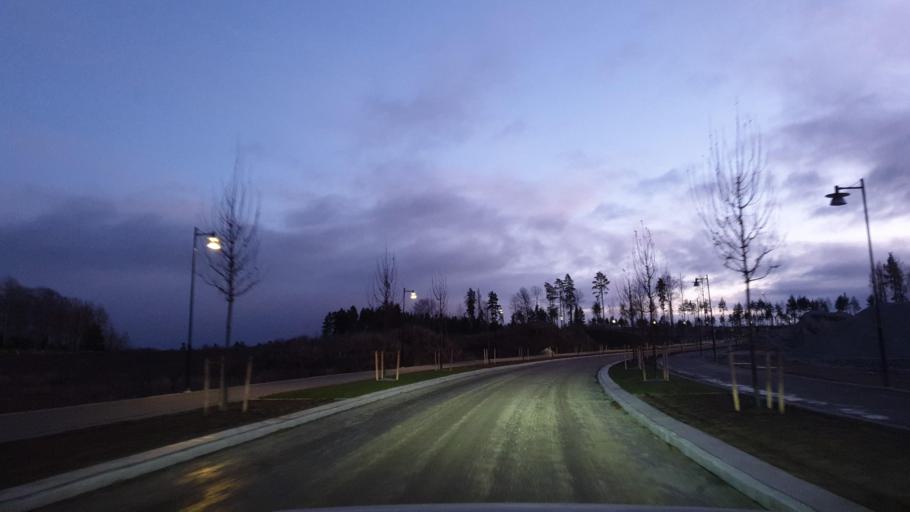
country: SE
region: Stockholm
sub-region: Sigtuna Kommun
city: Marsta
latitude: 59.6152
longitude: 17.7955
